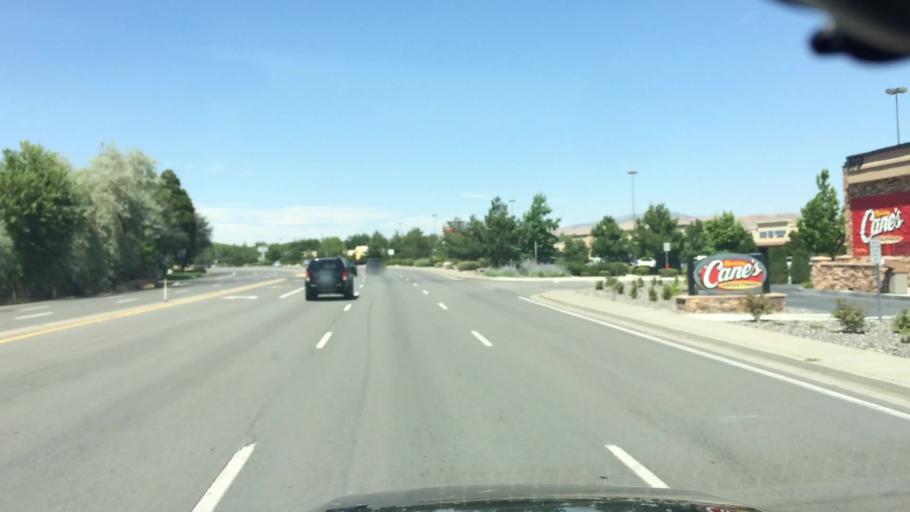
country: US
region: Nevada
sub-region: Washoe County
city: Sparks
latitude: 39.5384
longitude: -119.7349
